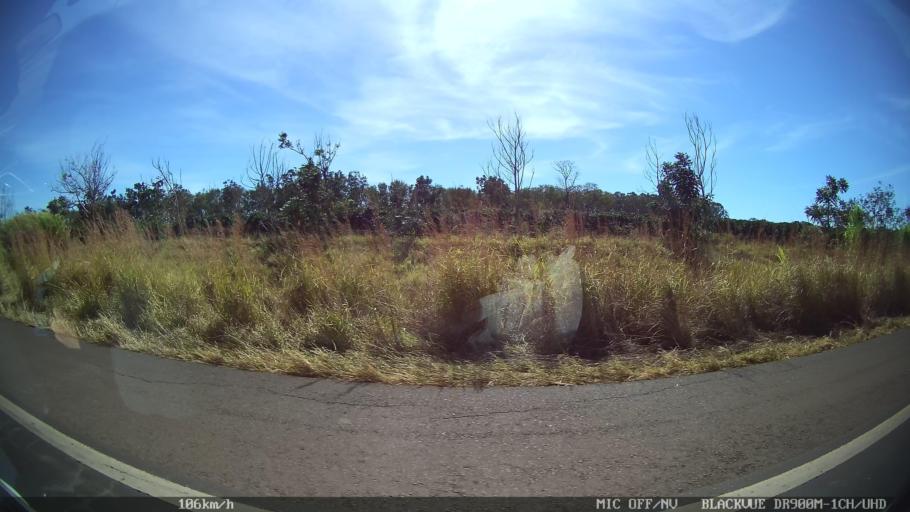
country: BR
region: Sao Paulo
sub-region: Franca
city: Franca
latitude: -20.5565
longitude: -47.5904
